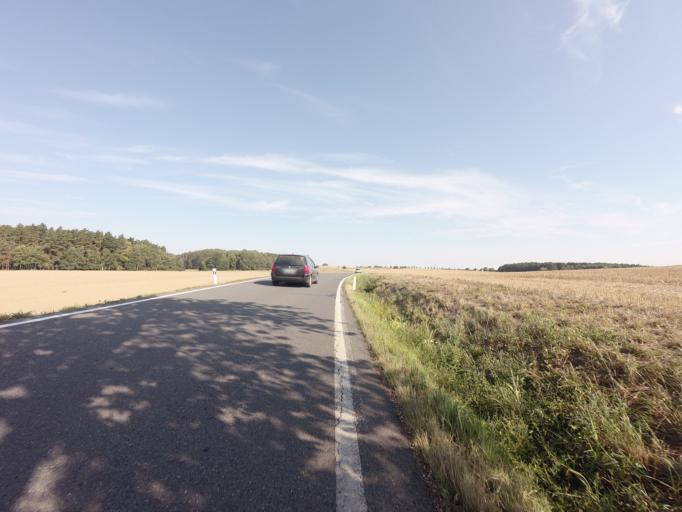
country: CZ
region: Jihocesky
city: Bernartice
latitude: 49.3132
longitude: 14.3731
